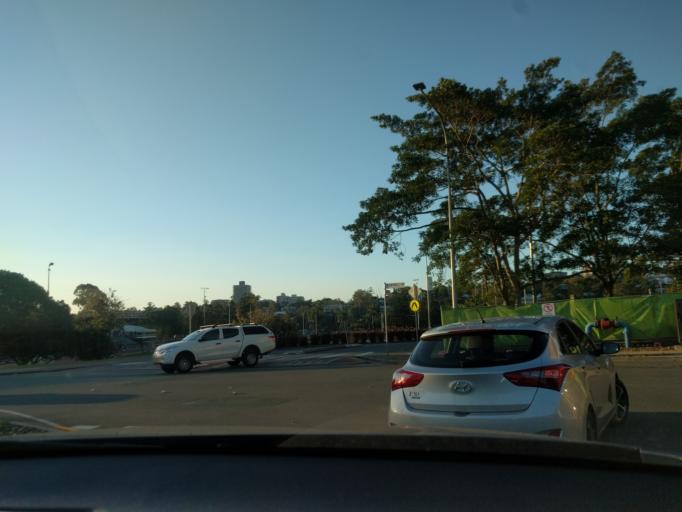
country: AU
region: Queensland
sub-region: Brisbane
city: South Brisbane
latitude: -27.4951
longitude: 153.0130
